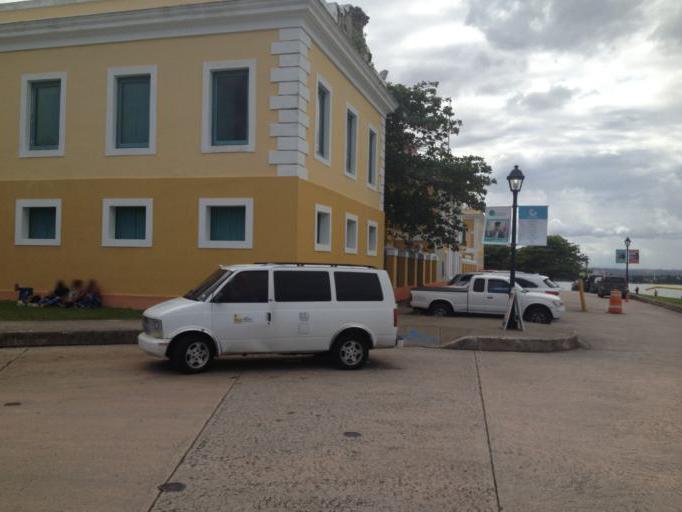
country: PR
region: San Juan
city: San Juan
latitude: 18.4683
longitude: -66.1211
